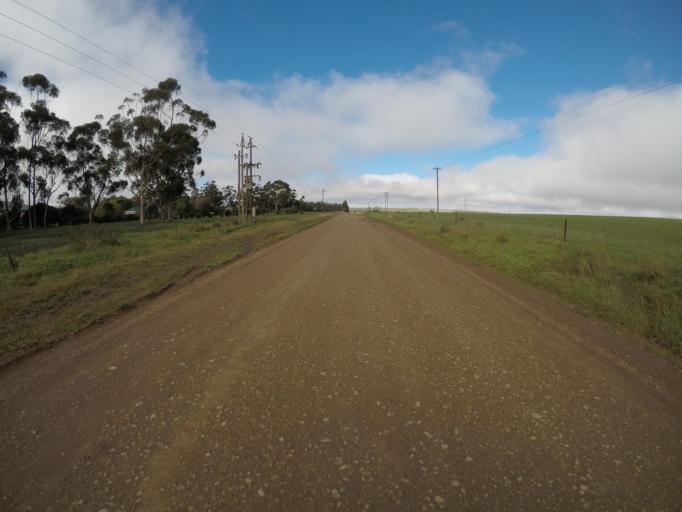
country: ZA
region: Western Cape
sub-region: Cape Winelands District Municipality
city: Ashton
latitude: -34.1387
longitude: 19.8610
